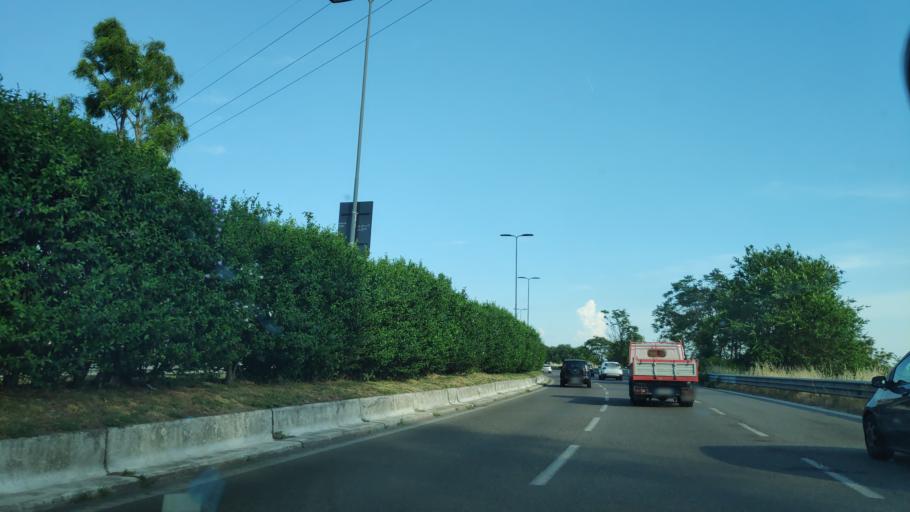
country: IT
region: Lombardy
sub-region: Citta metropolitana di Milano
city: Noverasco-Sporting Mirasole
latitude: 45.4233
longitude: 9.1980
